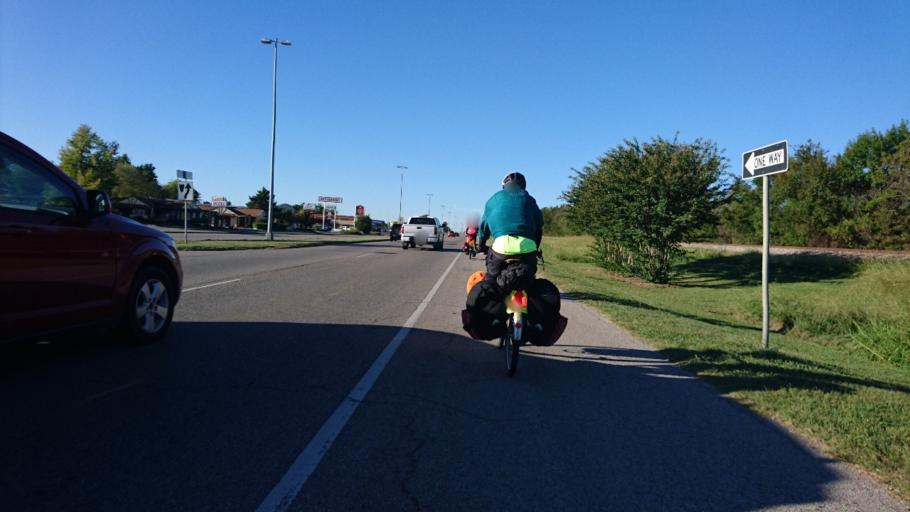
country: US
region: Oklahoma
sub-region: Rogers County
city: Claremore
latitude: 36.3030
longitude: -95.6243
